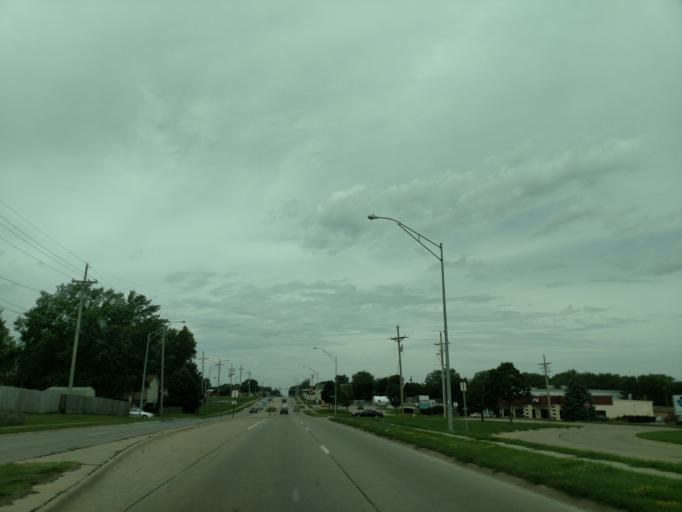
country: US
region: Nebraska
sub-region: Sarpy County
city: La Vista
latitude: 41.1909
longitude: -96.0353
